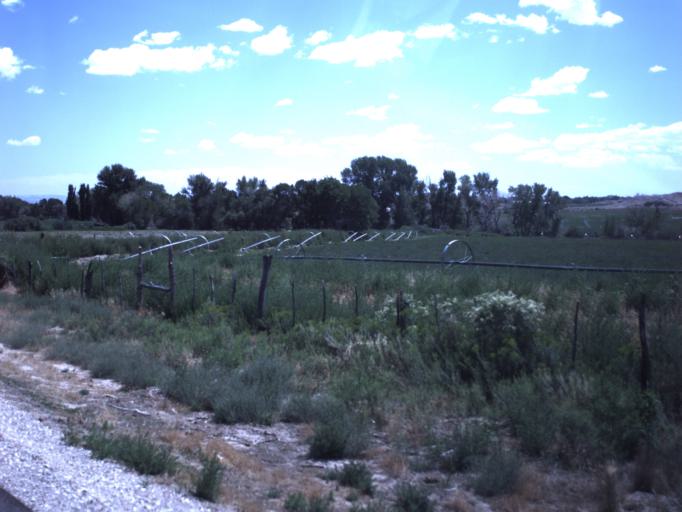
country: US
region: Utah
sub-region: Emery County
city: Orangeville
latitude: 39.2466
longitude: -111.0722
